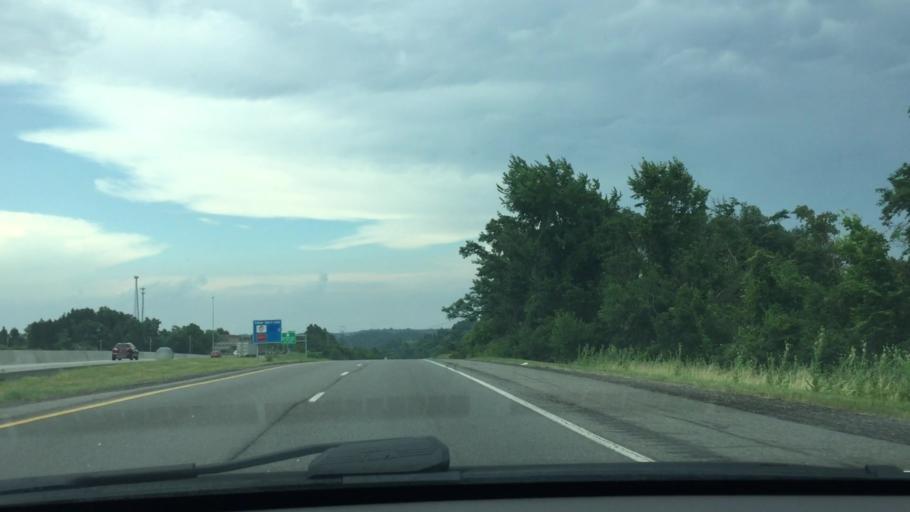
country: US
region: Ohio
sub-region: Belmont County
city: Saint Clairsville
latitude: 40.0689
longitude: -80.8482
